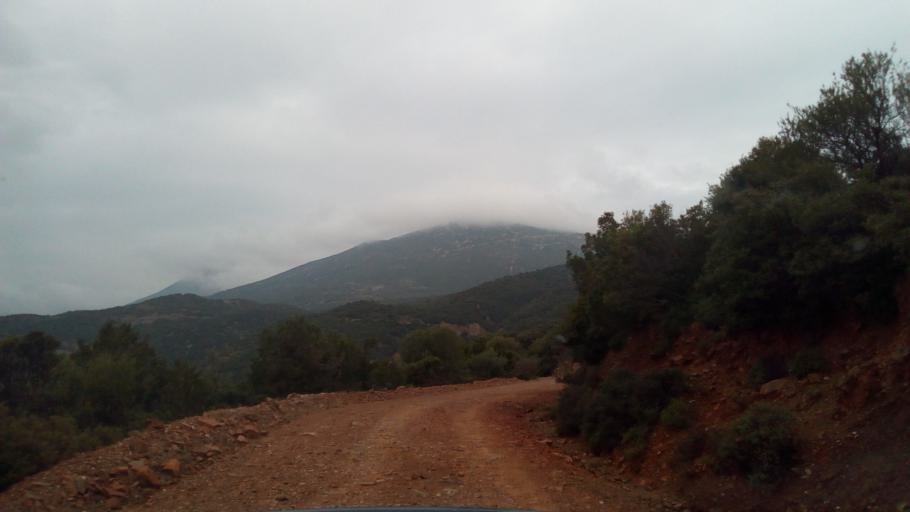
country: GR
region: West Greece
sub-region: Nomos Achaias
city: Temeni
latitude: 38.3637
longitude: 22.1590
